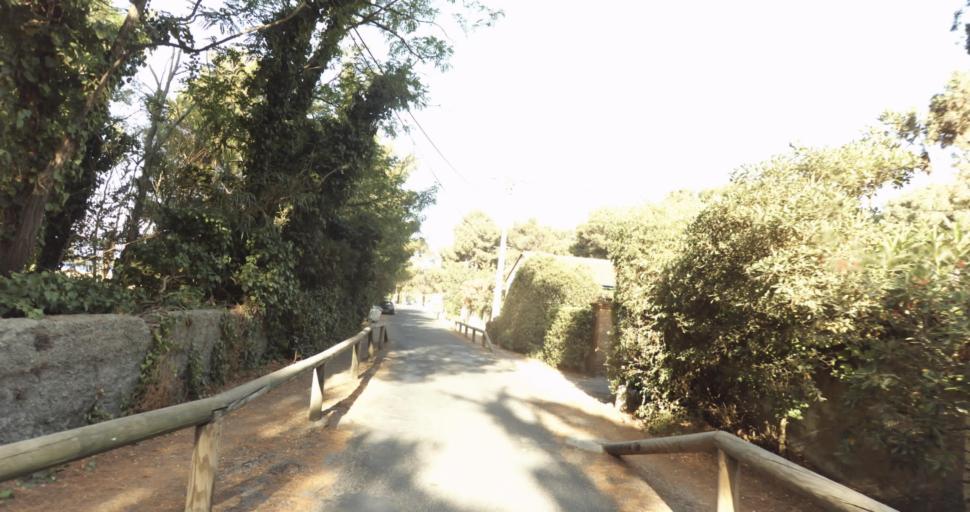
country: FR
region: Languedoc-Roussillon
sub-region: Departement des Pyrenees-Orientales
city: Saint-Cyprien-Plage
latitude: 42.6189
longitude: 3.0346
